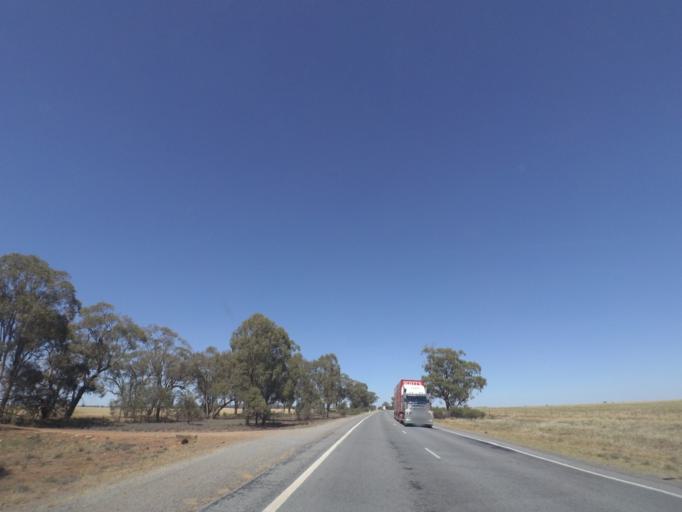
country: AU
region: New South Wales
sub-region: Narrandera
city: Narrandera
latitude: -34.4120
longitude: 146.8746
